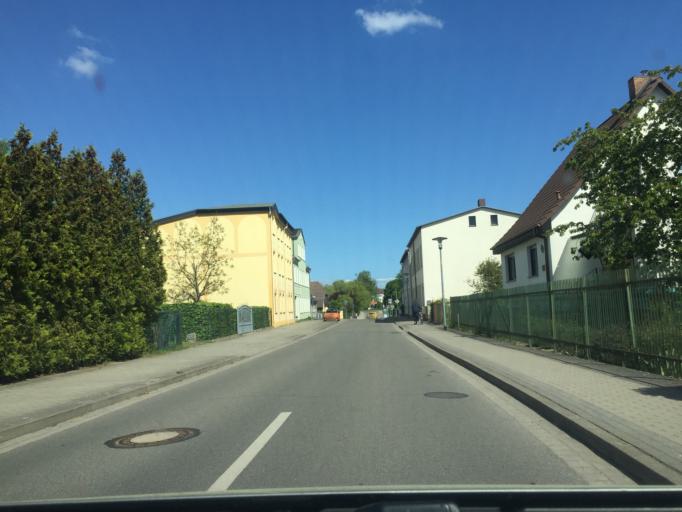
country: DE
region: Mecklenburg-Vorpommern
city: Torgelow
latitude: 53.6301
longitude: 14.0169
